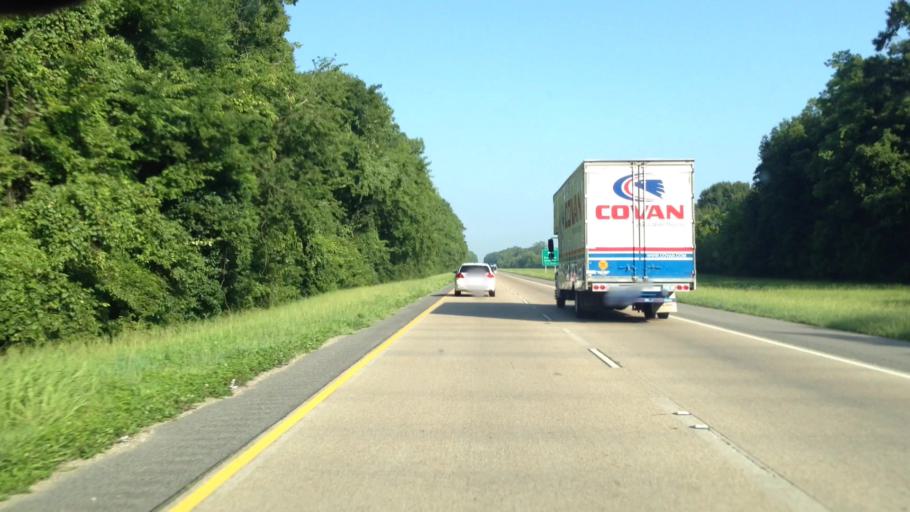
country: US
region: Louisiana
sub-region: Ascension Parish
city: Sorrento
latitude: 30.1806
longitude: -90.8953
